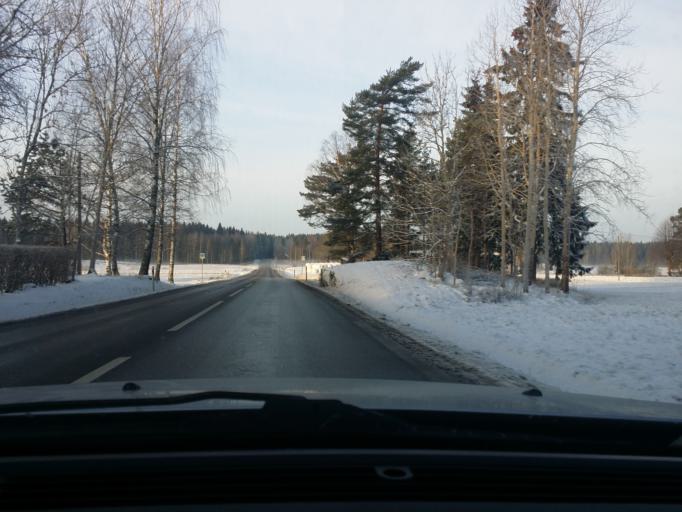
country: SE
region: OErebro
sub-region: Lindesbergs Kommun
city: Frovi
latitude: 59.5182
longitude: 15.3295
